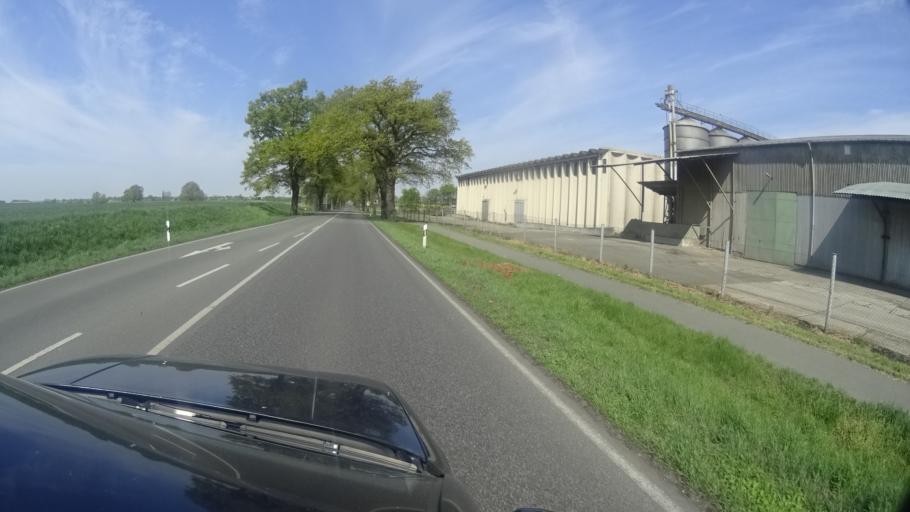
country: DE
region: Brandenburg
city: Retzow
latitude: 52.6371
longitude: 12.6926
